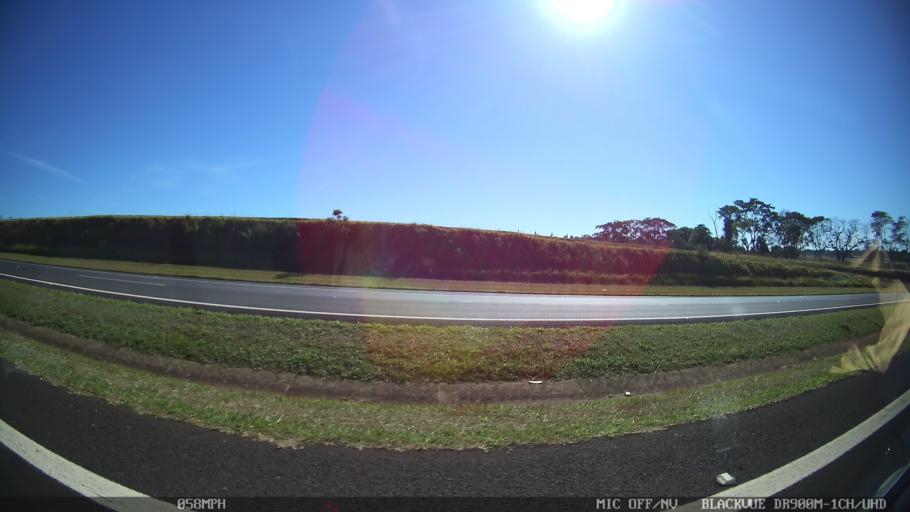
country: BR
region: Sao Paulo
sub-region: Franca
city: Franca
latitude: -20.5747
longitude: -47.3659
